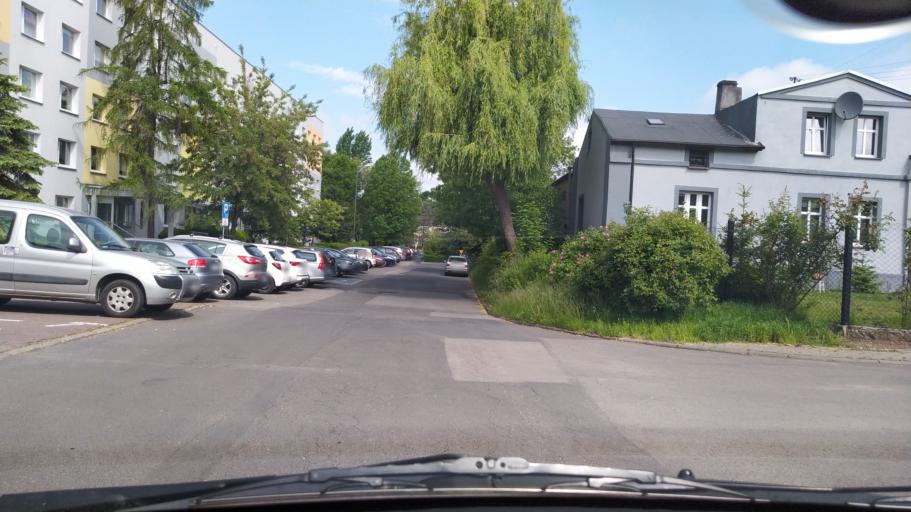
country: PL
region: Silesian Voivodeship
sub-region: Powiat gliwicki
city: Przyszowice
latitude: 50.2884
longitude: 18.7290
